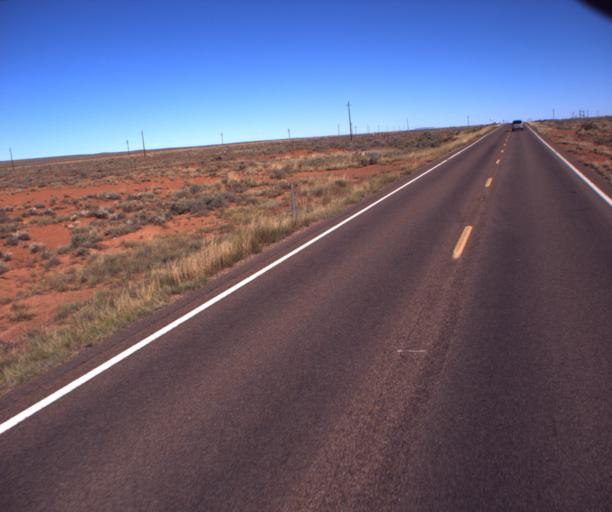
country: US
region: Arizona
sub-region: Navajo County
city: Holbrook
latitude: 34.7909
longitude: -110.1328
